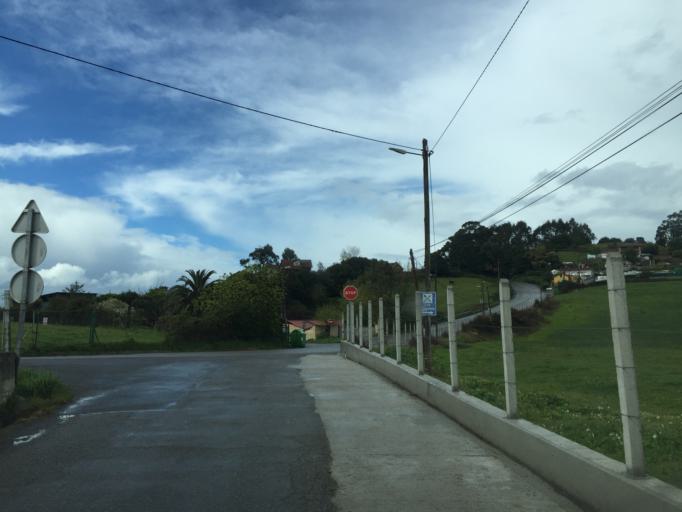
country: ES
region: Asturias
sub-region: Province of Asturias
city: Natahoyo
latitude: 43.5559
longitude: -5.7092
